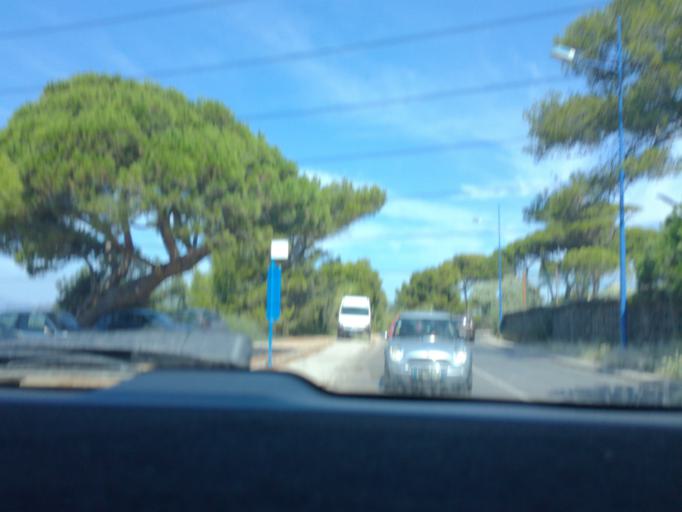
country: FR
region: Provence-Alpes-Cote d'Azur
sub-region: Departement du Var
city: Hyeres
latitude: 43.0563
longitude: 6.1470
